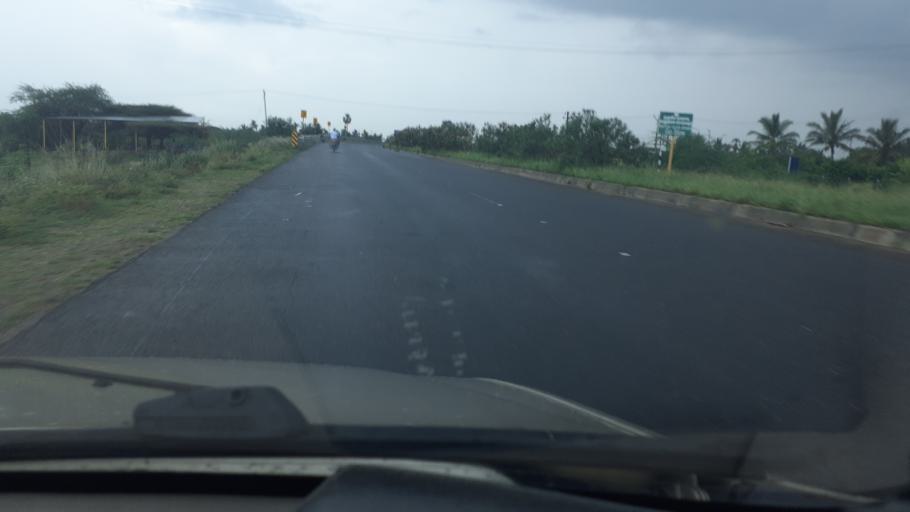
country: IN
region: Tamil Nadu
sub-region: Thoothukkudi
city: Kadambur
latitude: 9.0461
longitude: 77.7942
